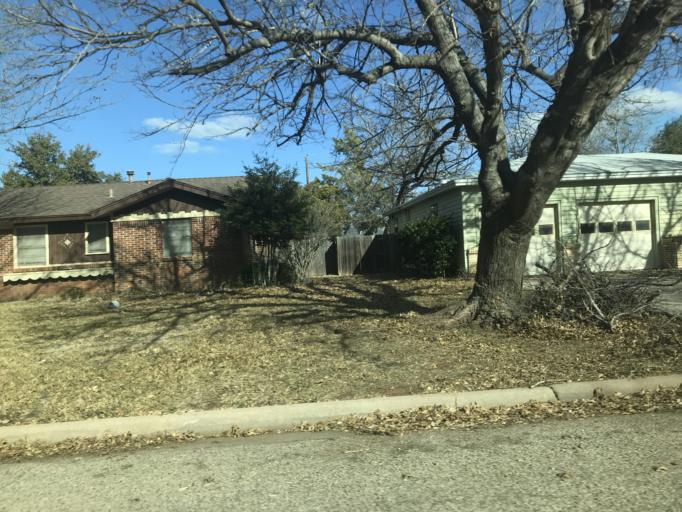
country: US
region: Texas
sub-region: Taylor County
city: Abilene
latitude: 32.4619
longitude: -99.7721
